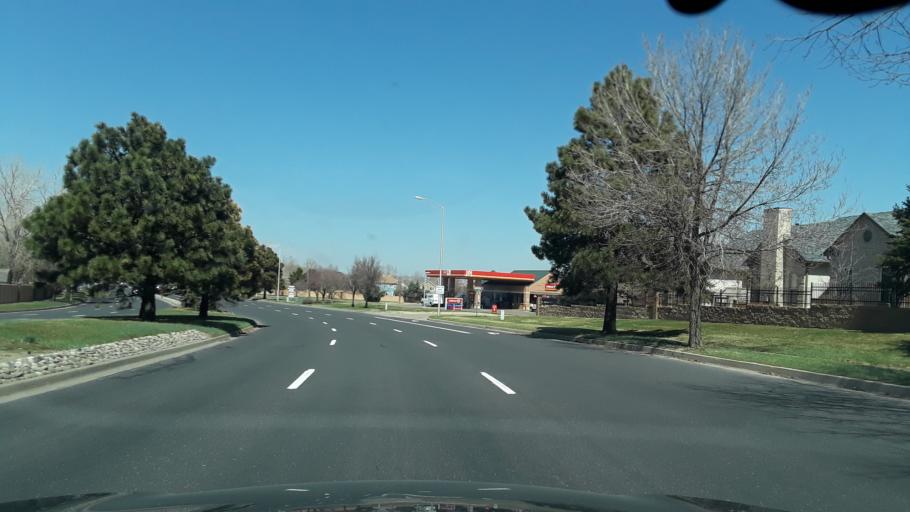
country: US
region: Colorado
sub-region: El Paso County
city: Cimarron Hills
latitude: 38.9144
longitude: -104.7335
